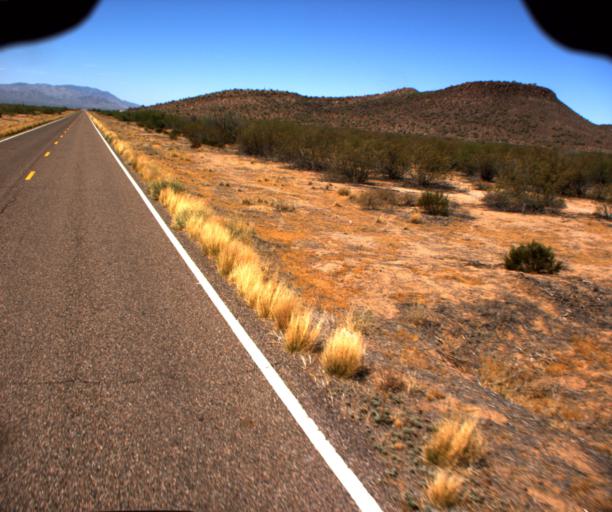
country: US
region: Arizona
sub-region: Yavapai County
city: Congress
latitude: 34.0158
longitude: -113.1020
